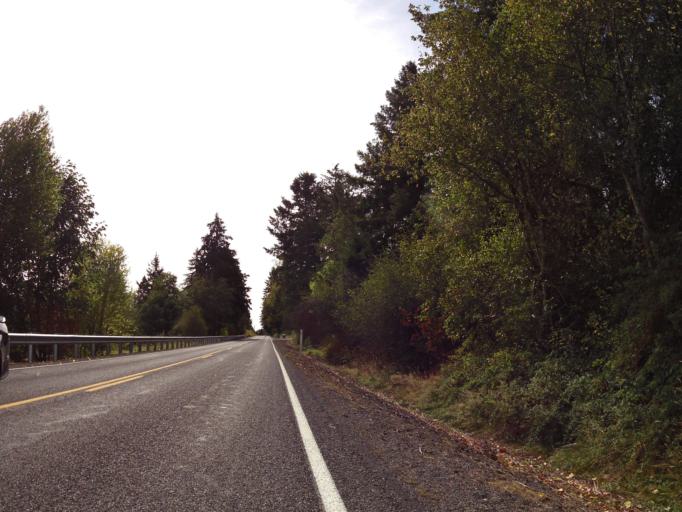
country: US
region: Washington
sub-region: Lewis County
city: Chehalis
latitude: 46.6354
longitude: -122.9712
